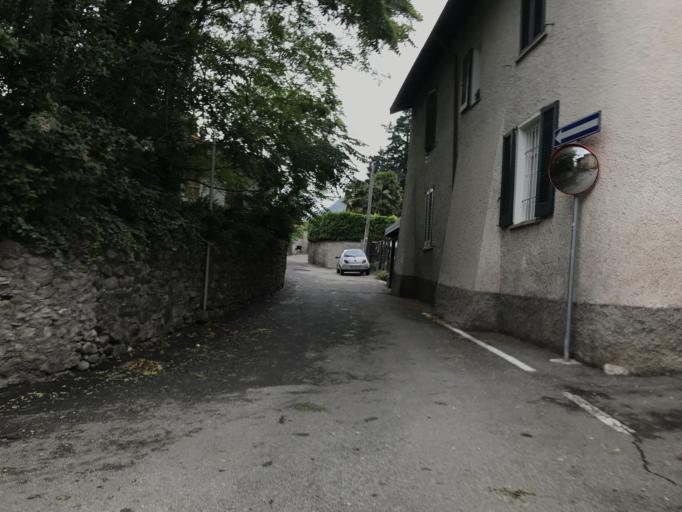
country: IT
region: Lombardy
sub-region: Provincia di Varese
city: Cittiglio
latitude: 45.8962
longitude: 8.6677
